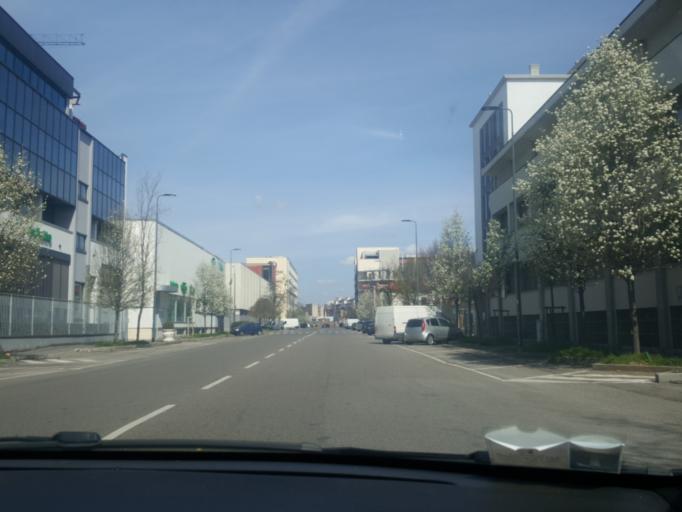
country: IT
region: Lombardy
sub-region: Citta metropolitana di Milano
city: Novate Milanese
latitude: 45.4981
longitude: 9.1390
